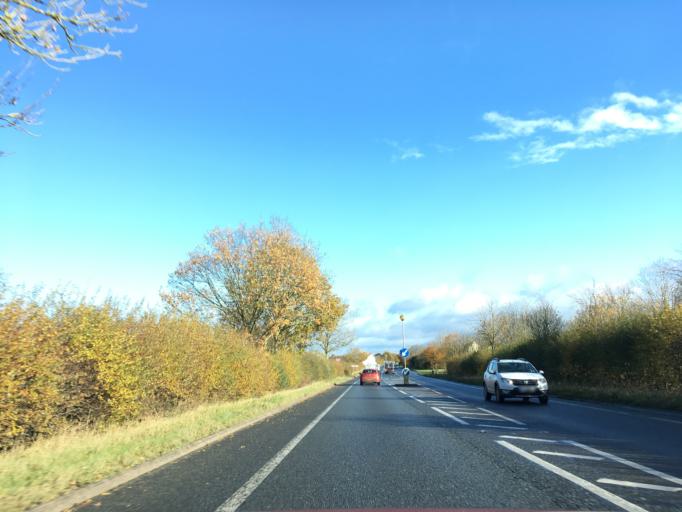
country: GB
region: England
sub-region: Gloucestershire
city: Gotherington
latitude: 52.0127
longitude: -2.0407
